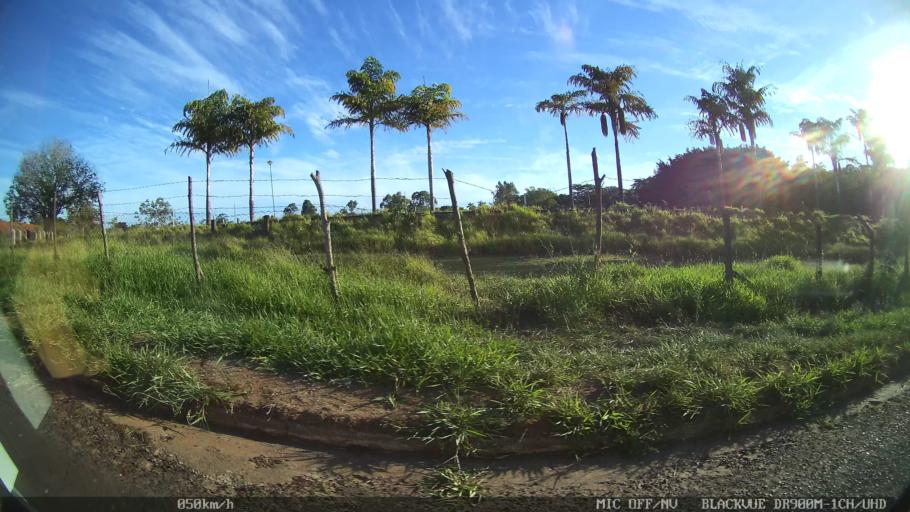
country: BR
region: Sao Paulo
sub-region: Sao Jose Do Rio Preto
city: Sao Jose do Rio Preto
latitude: -20.8606
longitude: -49.3356
